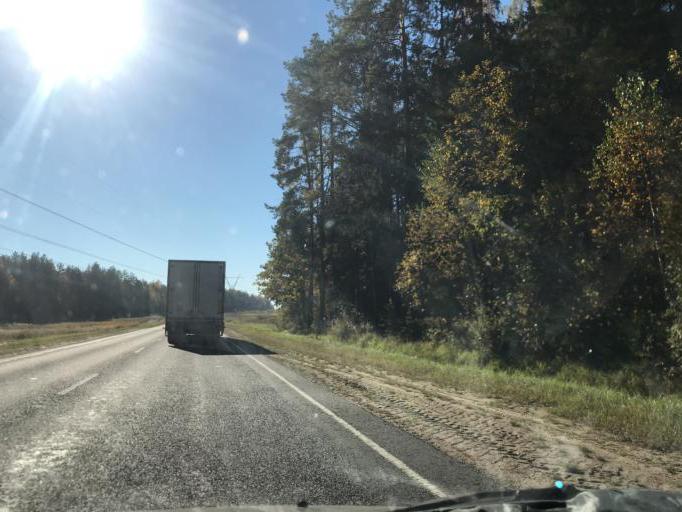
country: BY
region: Mogilev
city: Babruysk
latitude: 53.1160
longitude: 29.0536
